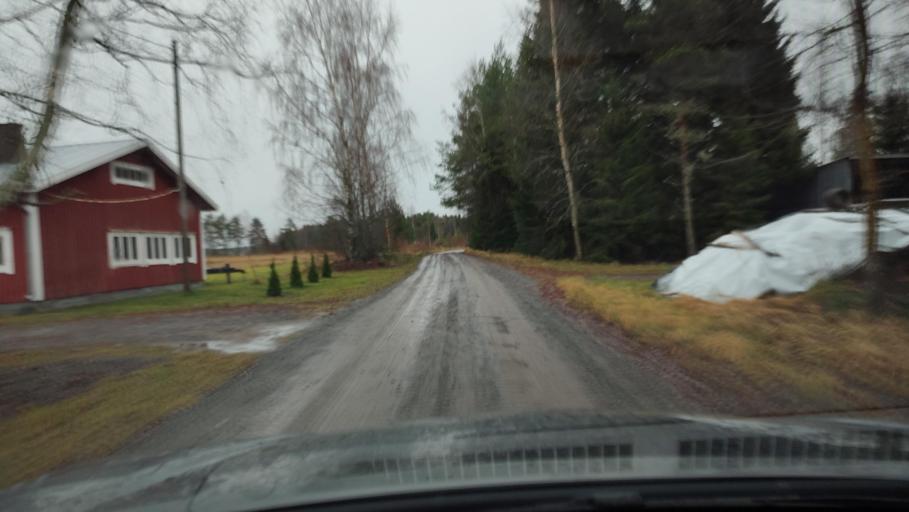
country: FI
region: Southern Ostrobothnia
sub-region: Suupohja
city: Karijoki
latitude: 62.2364
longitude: 21.5498
